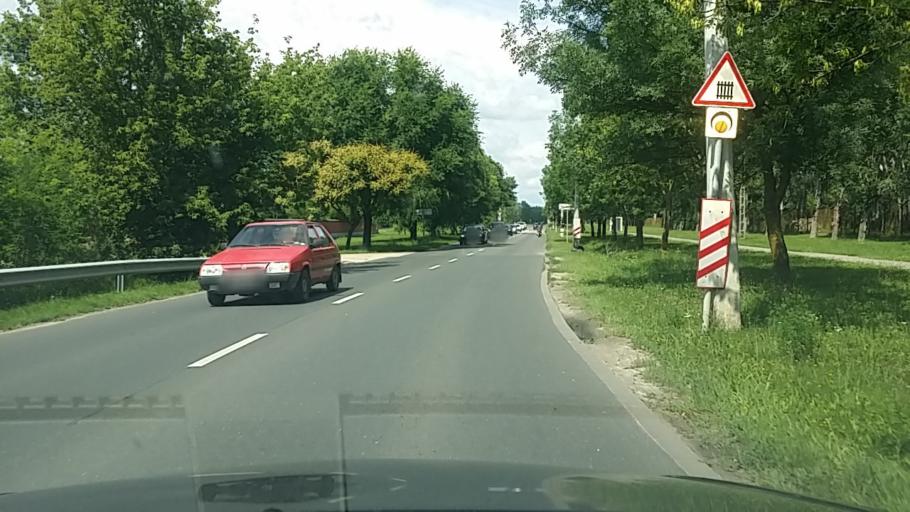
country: HU
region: Bacs-Kiskun
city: Kecskemet
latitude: 46.9058
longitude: 19.6498
